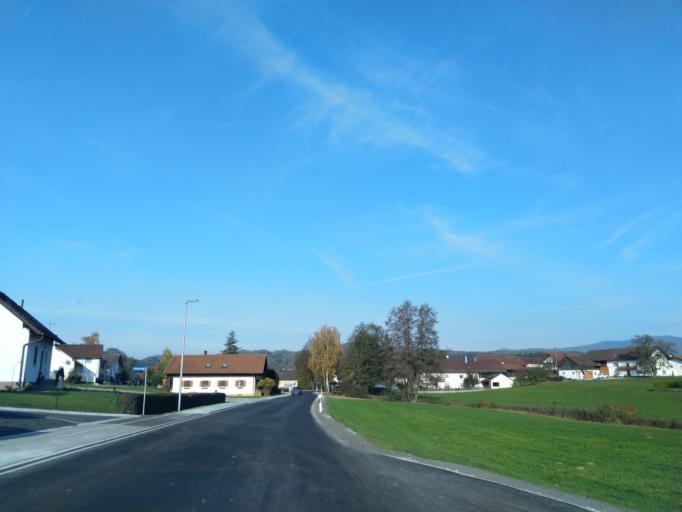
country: DE
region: Bavaria
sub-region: Lower Bavaria
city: Auerbach
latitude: 48.8045
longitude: 13.0919
